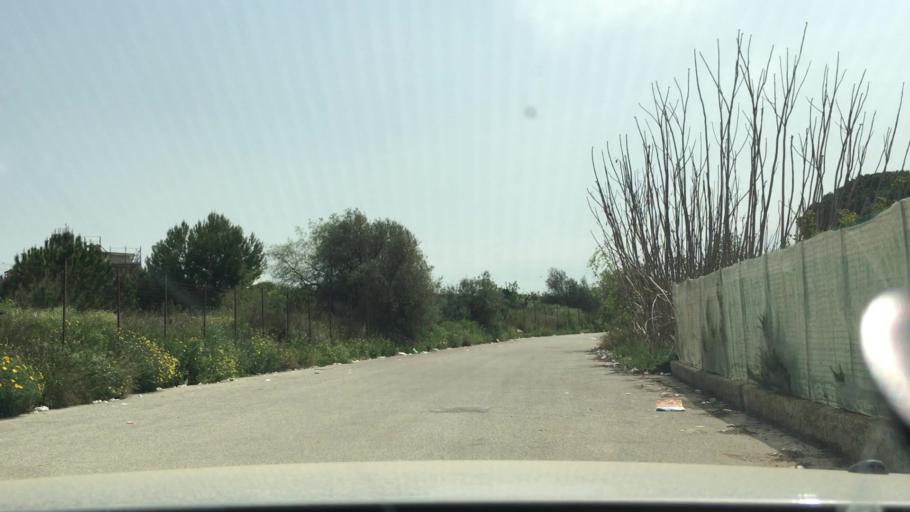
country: IT
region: Apulia
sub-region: Provincia di Barletta - Andria - Trani
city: Capirro
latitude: 41.2583
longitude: 16.4528
